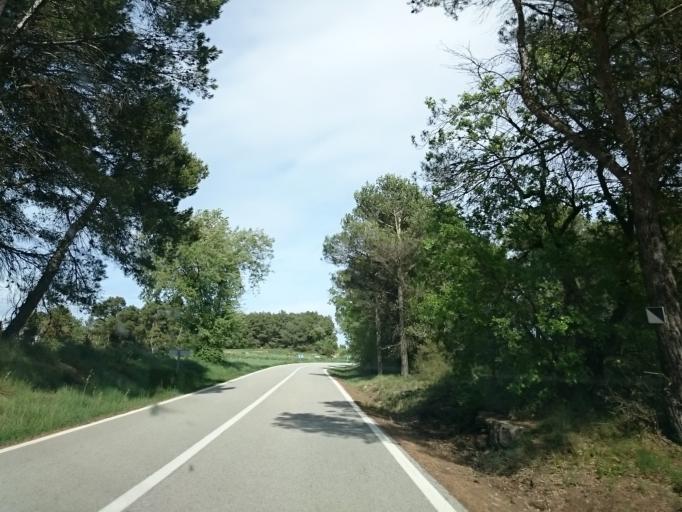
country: ES
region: Catalonia
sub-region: Provincia de Barcelona
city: Bellprat
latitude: 41.5691
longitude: 1.4542
